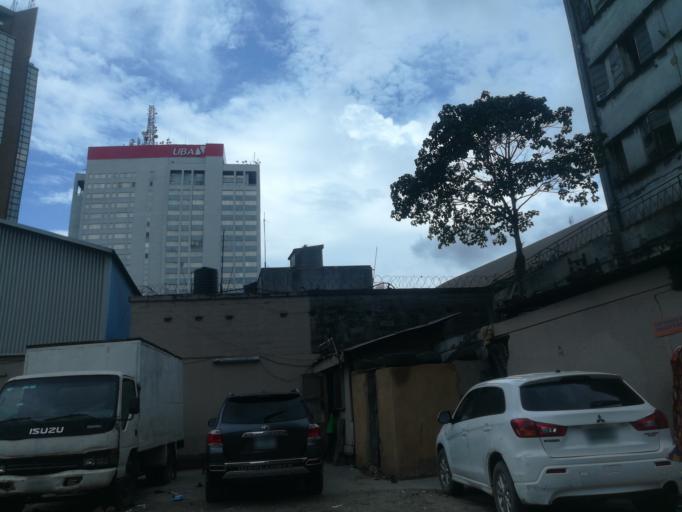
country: NG
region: Lagos
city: Lagos
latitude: 6.4550
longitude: 3.3848
